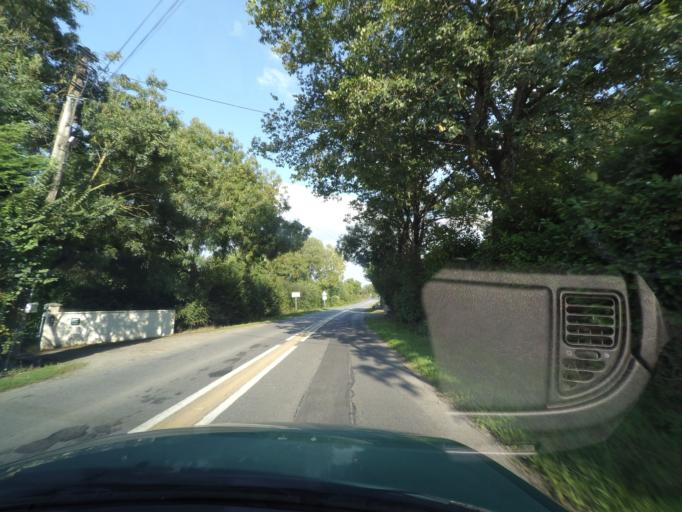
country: FR
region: Pays de la Loire
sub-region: Departement de la Loire-Atlantique
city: Saint-Philbert-de-Grand-Lieu
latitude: 47.0349
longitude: -1.6673
